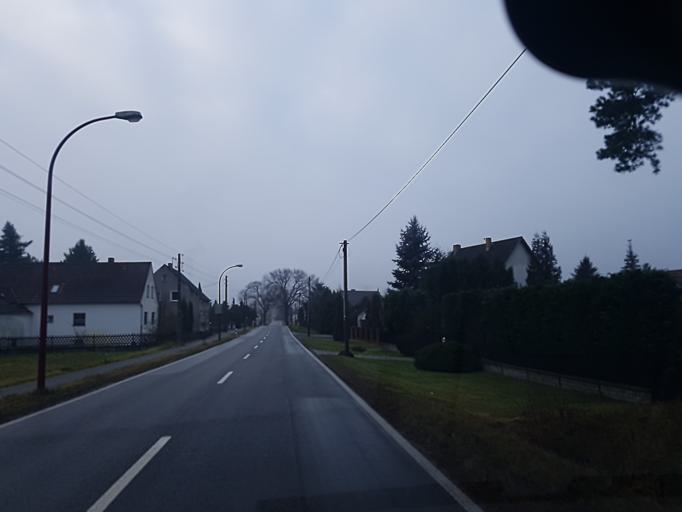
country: DE
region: Brandenburg
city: Finsterwalde
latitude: 51.5899
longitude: 13.7053
